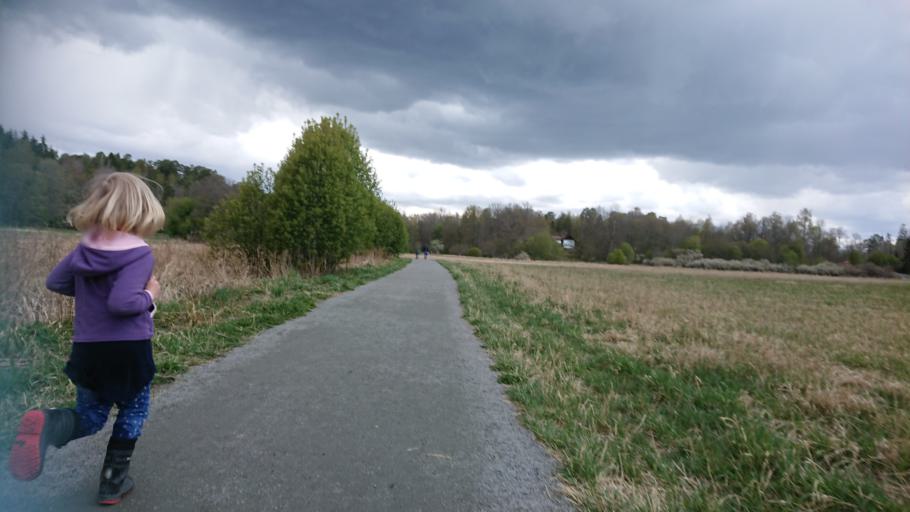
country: SE
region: Uppsala
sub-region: Uppsala Kommun
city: Uppsala
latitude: 59.7972
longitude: 17.6091
